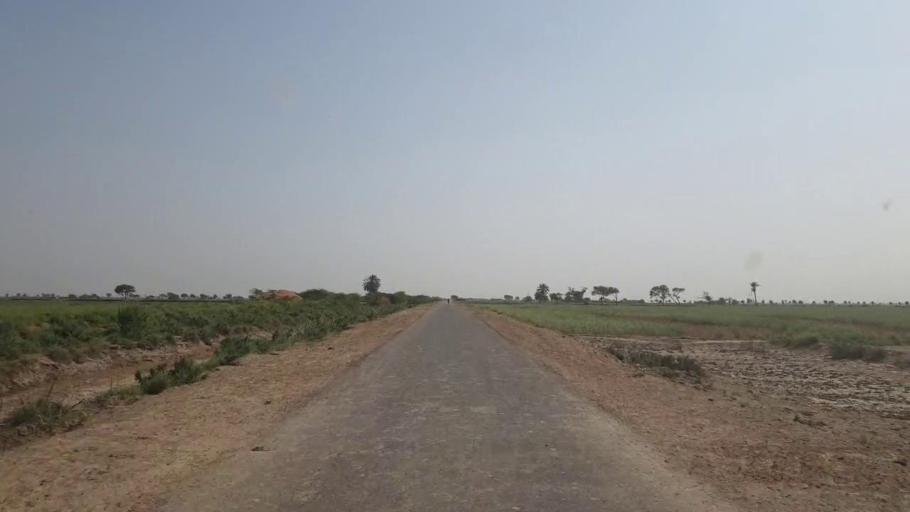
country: PK
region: Sindh
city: Jati
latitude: 24.4572
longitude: 68.5131
